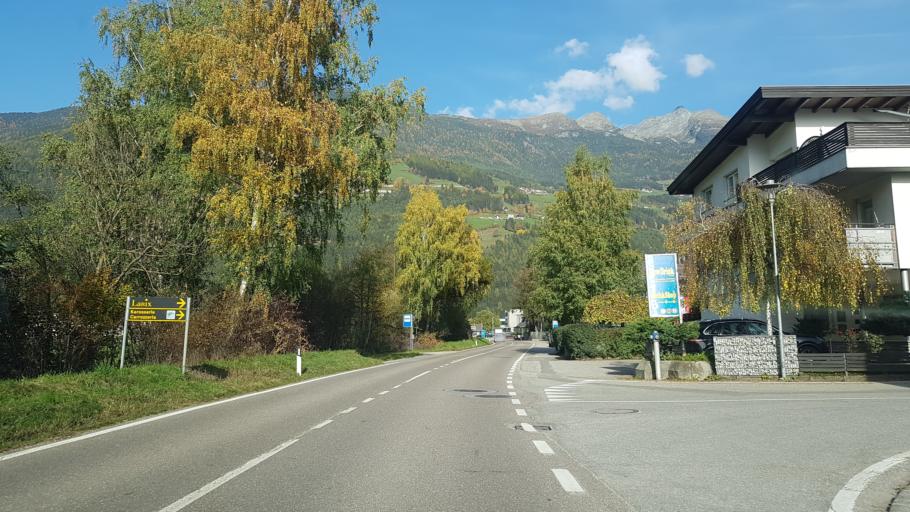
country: IT
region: Trentino-Alto Adige
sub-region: Bolzano
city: Campo Tures
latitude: 46.9079
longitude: 11.9586
